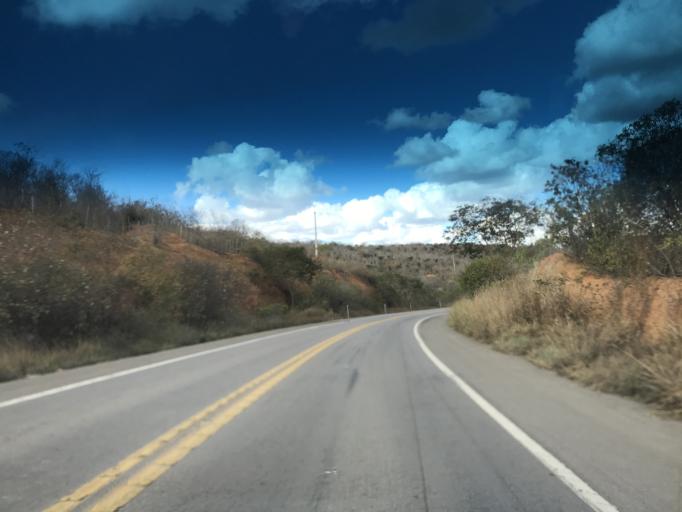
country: BR
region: Bahia
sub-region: Andarai
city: Vera Cruz
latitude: -12.4674
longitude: -41.0938
